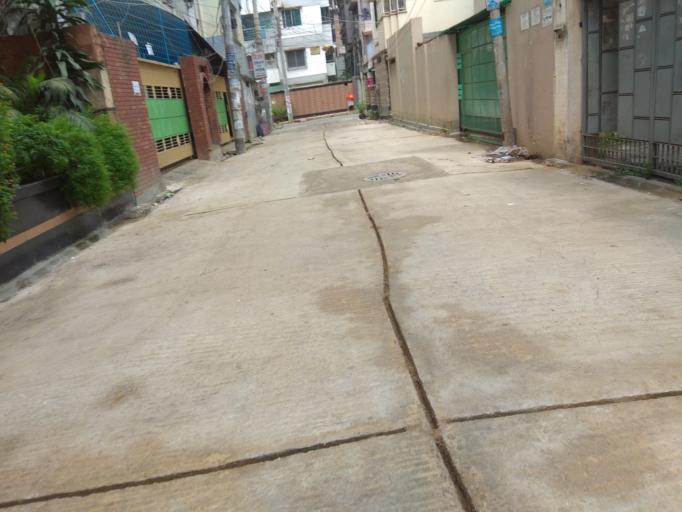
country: BD
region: Dhaka
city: Azimpur
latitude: 23.8030
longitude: 90.3566
